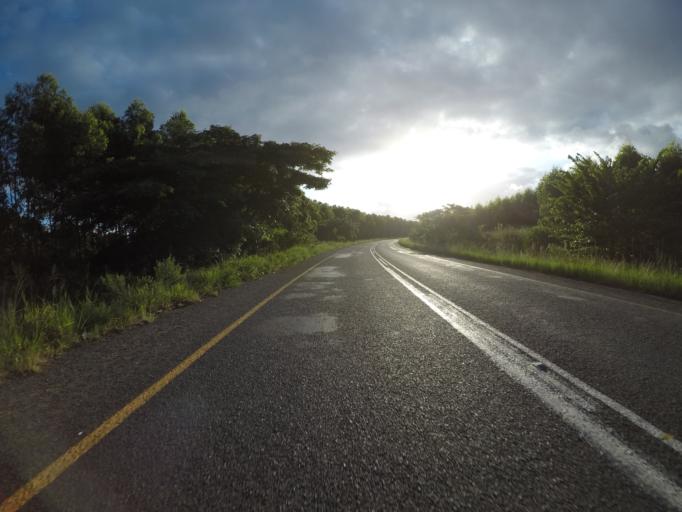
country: ZA
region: KwaZulu-Natal
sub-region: uMkhanyakude District Municipality
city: Mtubatuba
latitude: -28.4121
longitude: 32.1938
